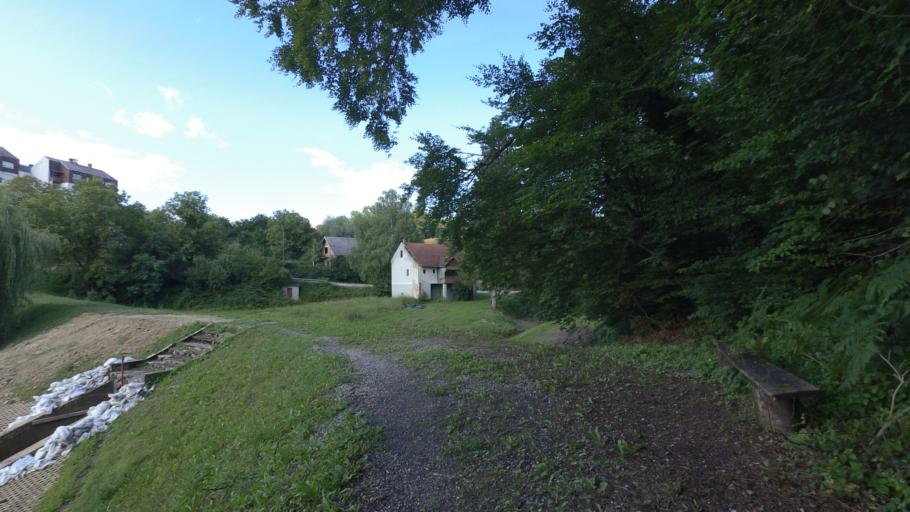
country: HR
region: Sisacko-Moslavacka
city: Gvozd
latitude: 45.2977
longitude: 15.9708
